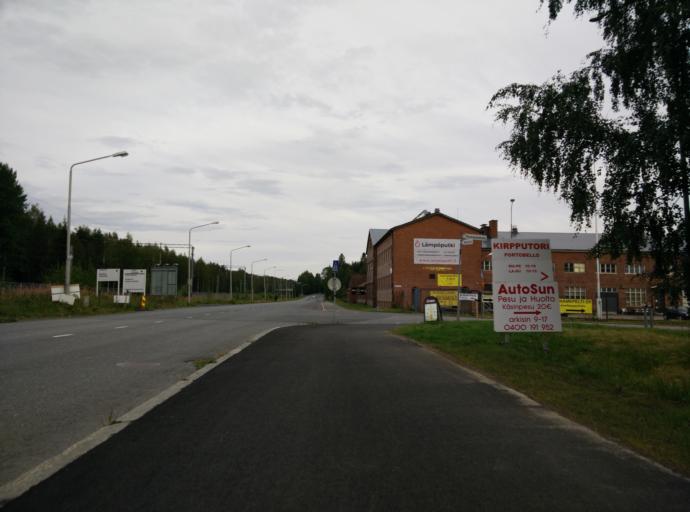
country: FI
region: Haeme
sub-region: Haemeenlinna
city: Haemeenlinna
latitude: 60.9876
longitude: 24.4976
